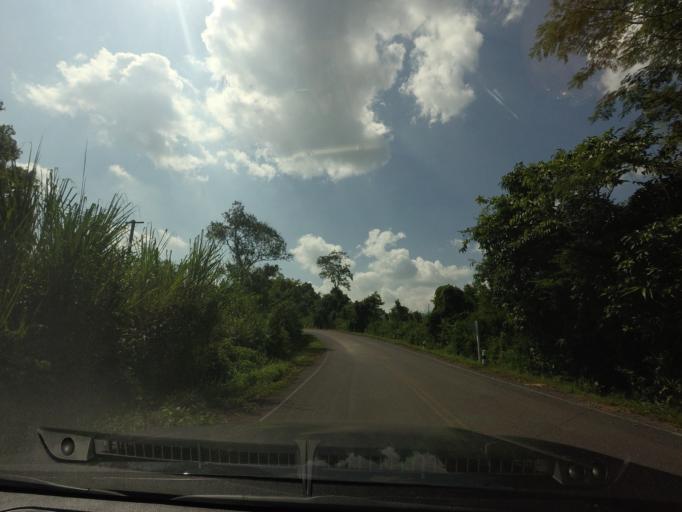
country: TH
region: Nan
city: Bo Kluea
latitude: 19.0755
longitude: 101.1359
